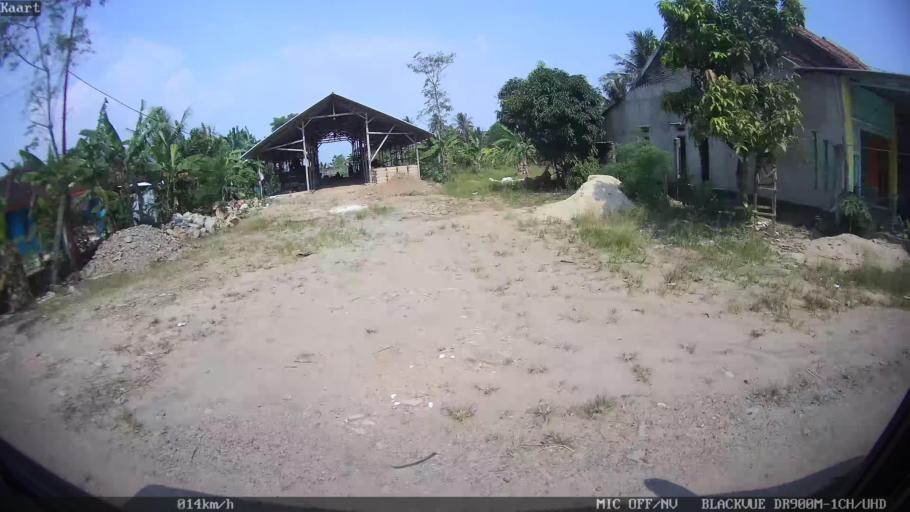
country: ID
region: Lampung
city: Natar
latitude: -5.3001
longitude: 105.2244
